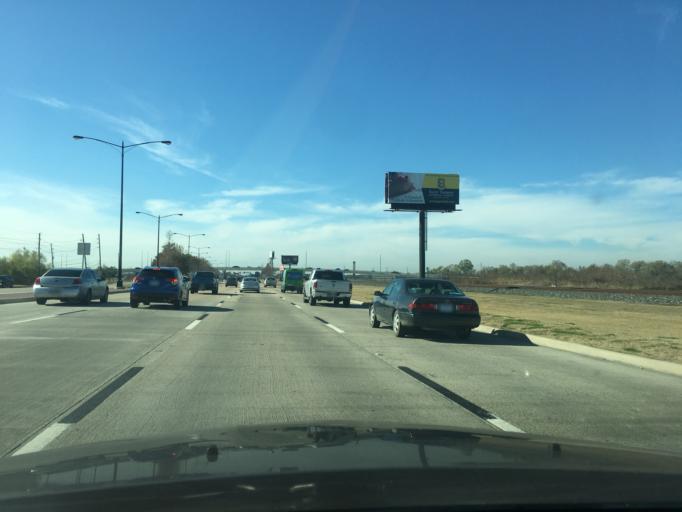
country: US
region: Texas
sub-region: Fort Bend County
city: Sugar Land
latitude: 29.6160
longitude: -95.6447
